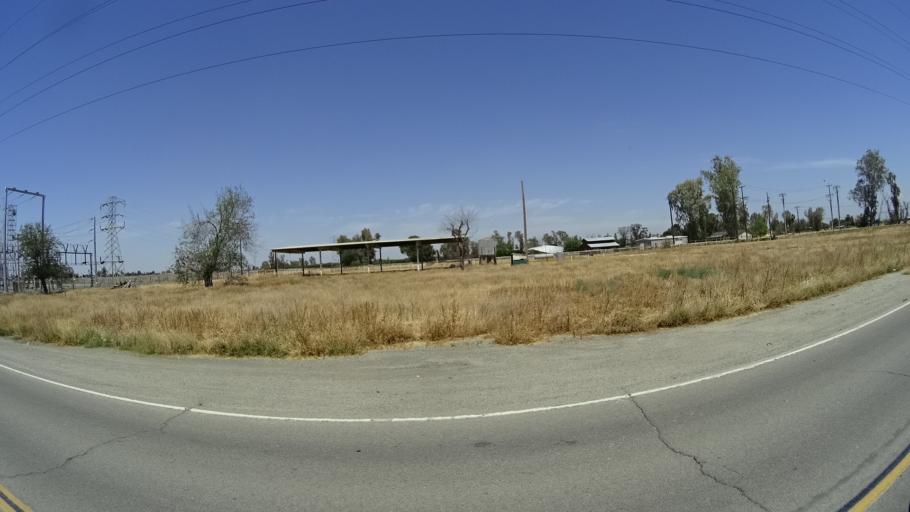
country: US
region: California
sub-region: Kings County
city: Corcoran
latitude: 36.1089
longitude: -119.5562
